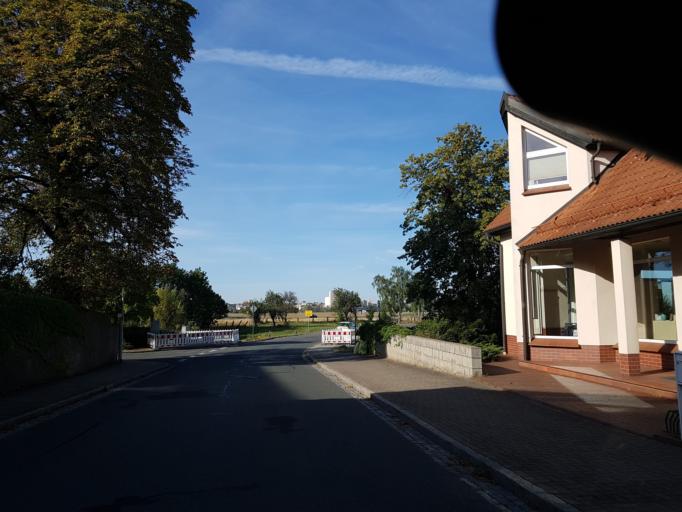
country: DE
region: Saxony
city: Zeithain
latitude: 51.3199
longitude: 13.3162
